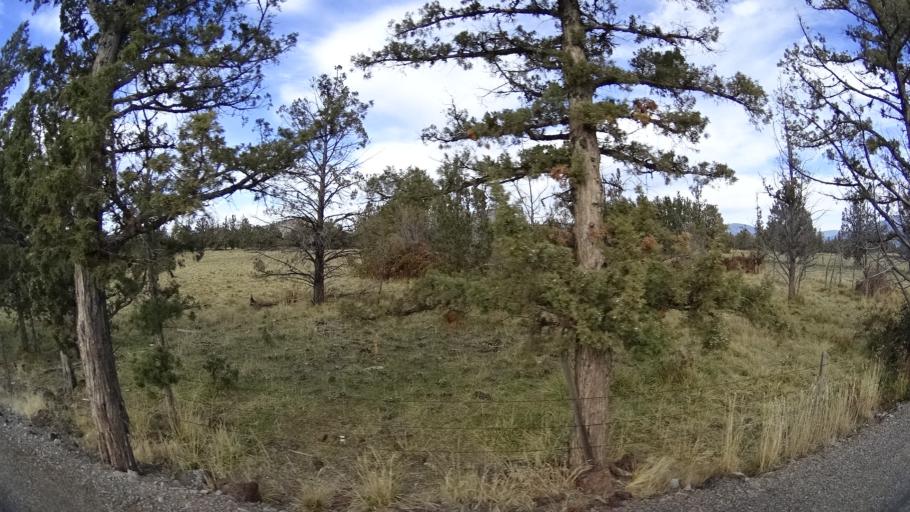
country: US
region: California
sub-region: Siskiyou County
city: Montague
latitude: 41.6385
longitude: -122.4293
